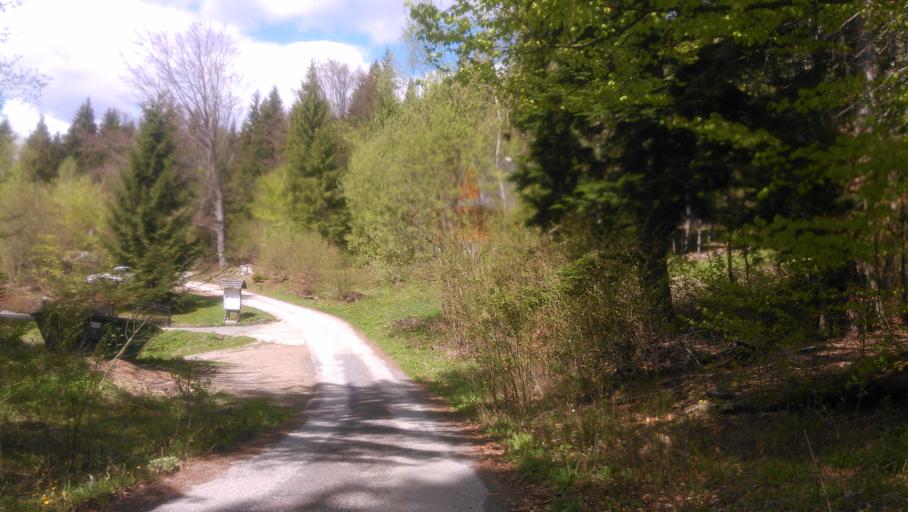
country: SK
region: Banskobystricky
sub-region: Okres Banska Bystrica
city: Brezno
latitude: 48.8764
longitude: 19.5906
